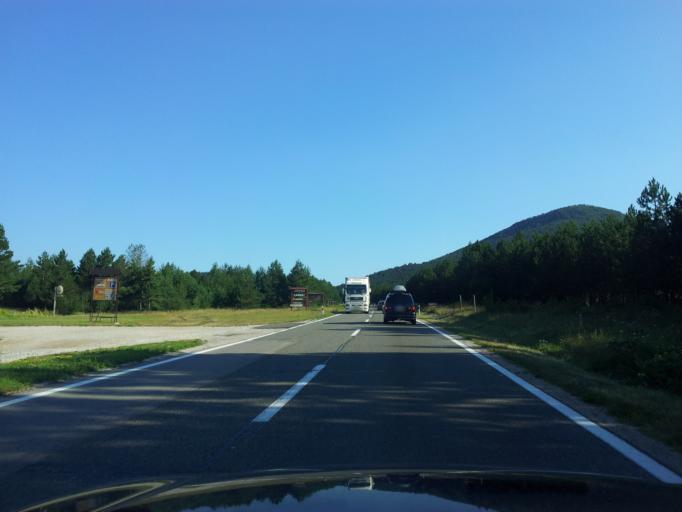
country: HR
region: Licko-Senjska
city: Jezerce
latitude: 44.7737
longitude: 15.6911
